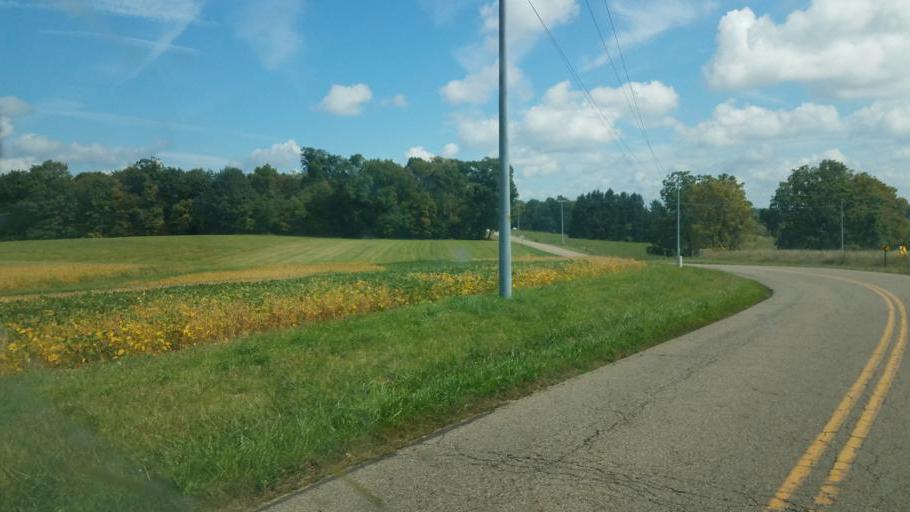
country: US
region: Ohio
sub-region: Knox County
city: Fredericktown
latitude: 40.4959
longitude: -82.4413
